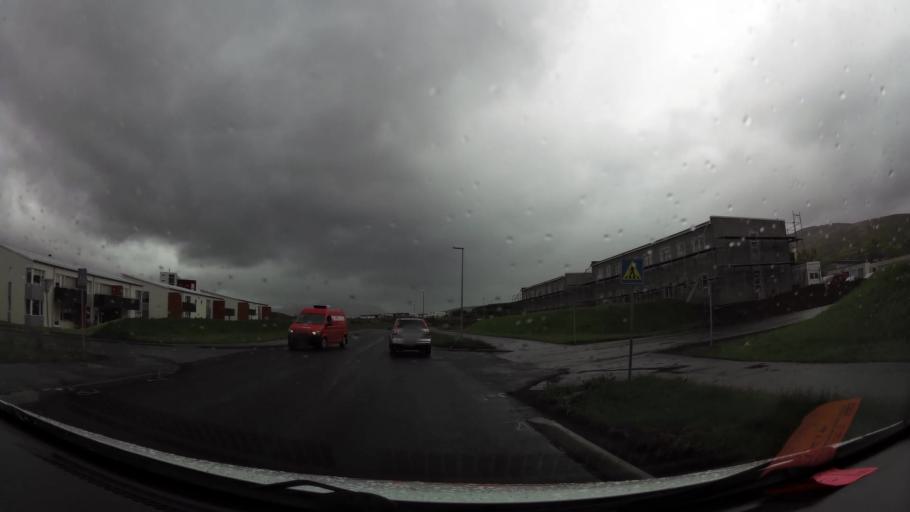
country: IS
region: Northeast
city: Akureyri
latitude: 65.6674
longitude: -18.1079
